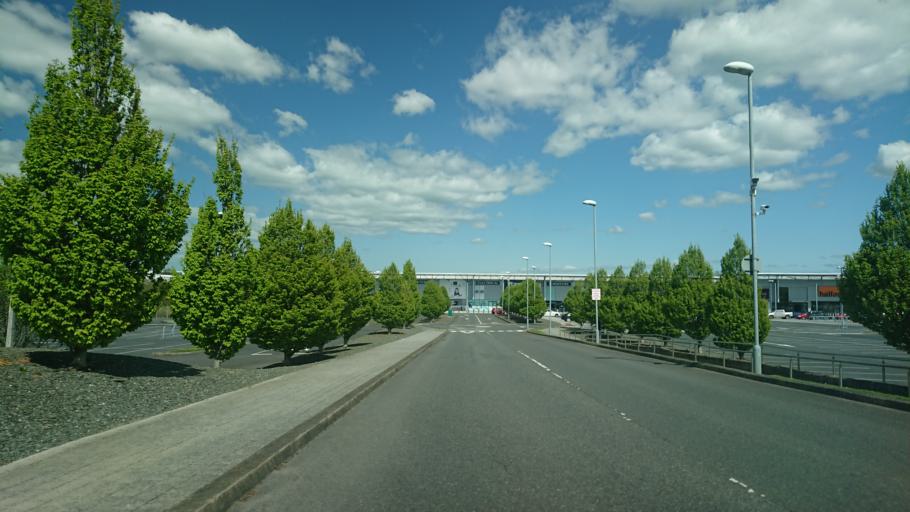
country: IE
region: Munster
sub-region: Waterford
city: Waterford
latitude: 52.2451
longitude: -7.1707
